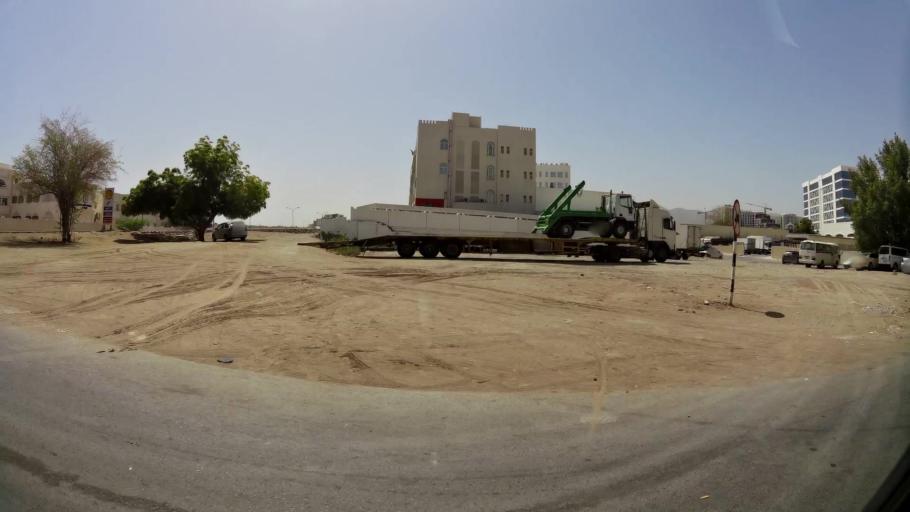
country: OM
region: Muhafazat Masqat
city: Bawshar
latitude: 23.5961
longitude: 58.4090
